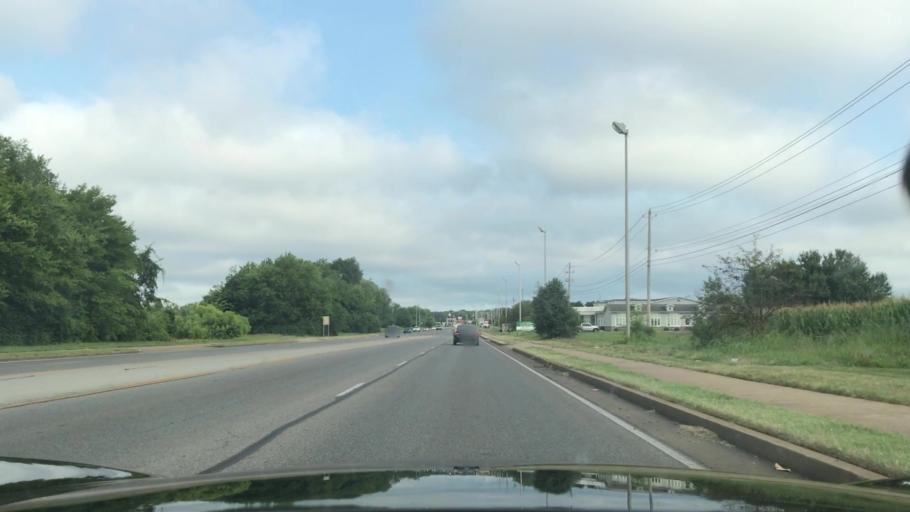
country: US
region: Kentucky
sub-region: Warren County
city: Bowling Green
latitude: 36.9548
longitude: -86.4450
